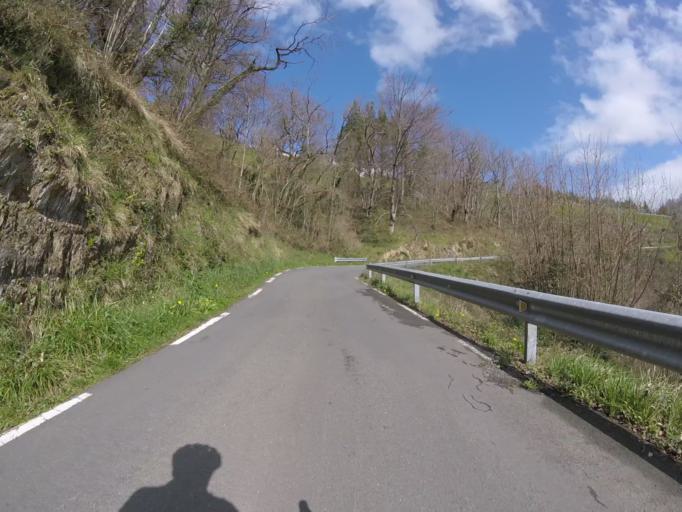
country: ES
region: Basque Country
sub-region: Provincia de Guipuzcoa
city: Tolosa
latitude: 43.1302
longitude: -2.1054
